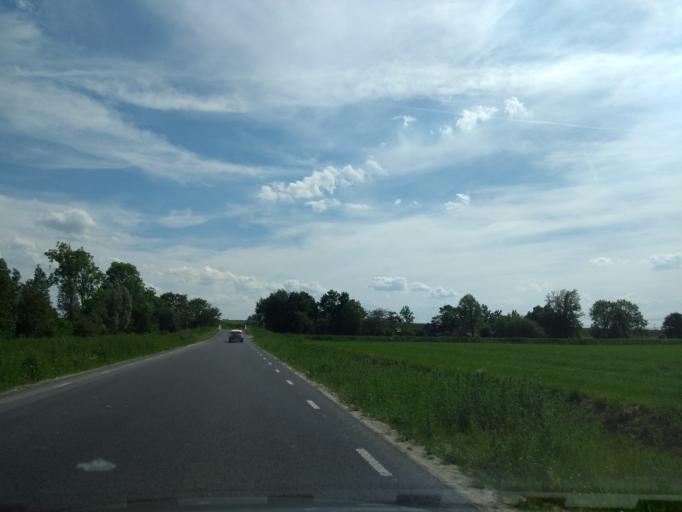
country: NL
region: Groningen
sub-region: Gemeente Zuidhorn
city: Aduard
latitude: 53.2481
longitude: 6.4798
